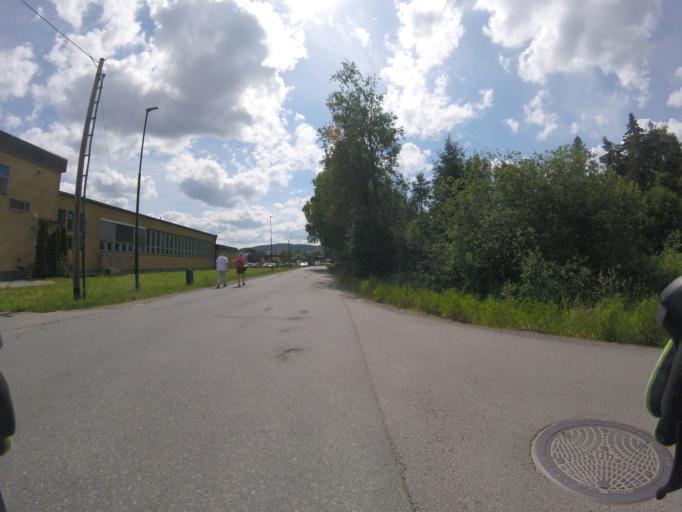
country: NO
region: Akershus
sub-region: Skedsmo
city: Lillestrom
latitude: 59.9607
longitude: 11.0206
